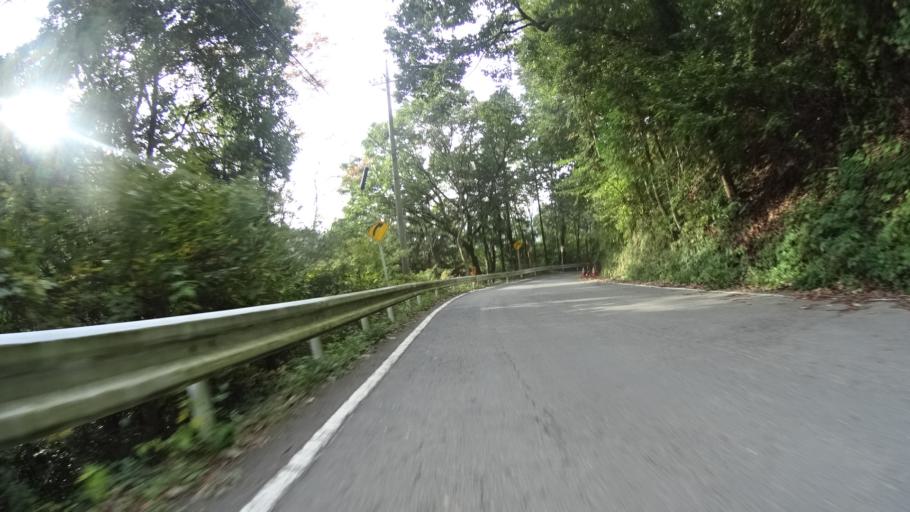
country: JP
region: Yamanashi
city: Uenohara
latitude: 35.6790
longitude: 139.0971
